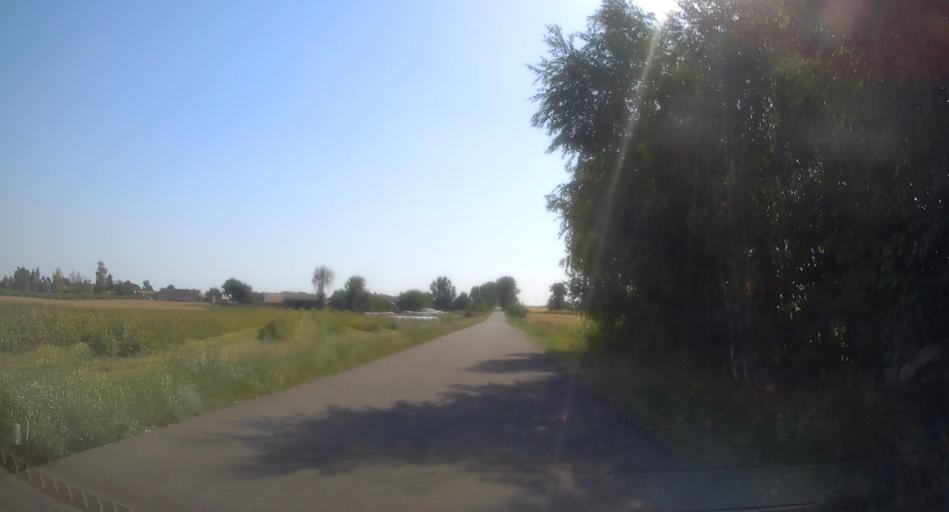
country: PL
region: Lodz Voivodeship
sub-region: Powiat skierniewicki
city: Kaweczyn Nowy
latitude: 51.8783
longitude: 20.2150
